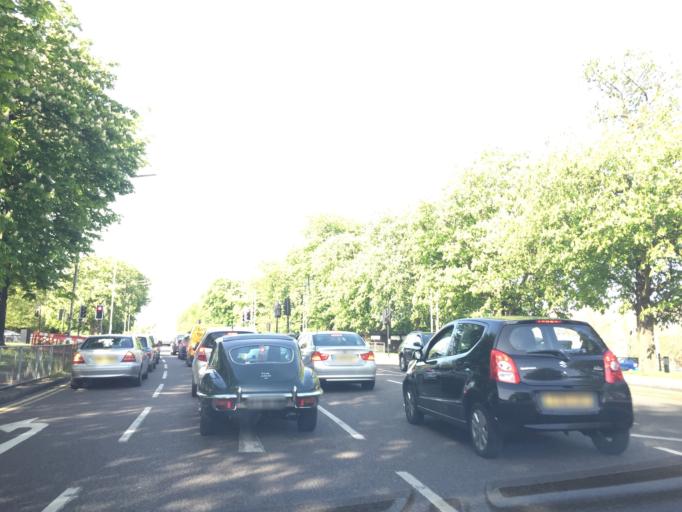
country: GB
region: England
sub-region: Greater London
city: Woodford Green
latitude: 51.6069
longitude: 0.0194
